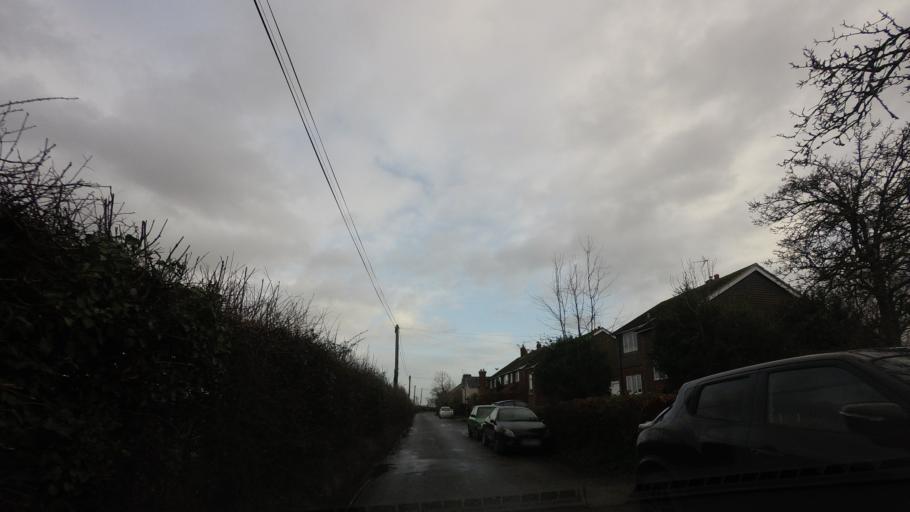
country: GB
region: England
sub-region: Kent
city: Hadlow
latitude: 51.2251
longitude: 0.3118
